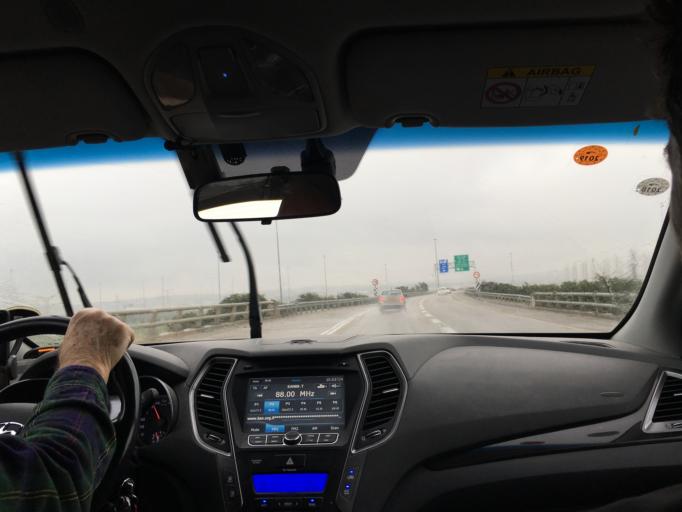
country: IL
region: Central District
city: Rosh Ha'Ayin
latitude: 32.1155
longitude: 34.9342
